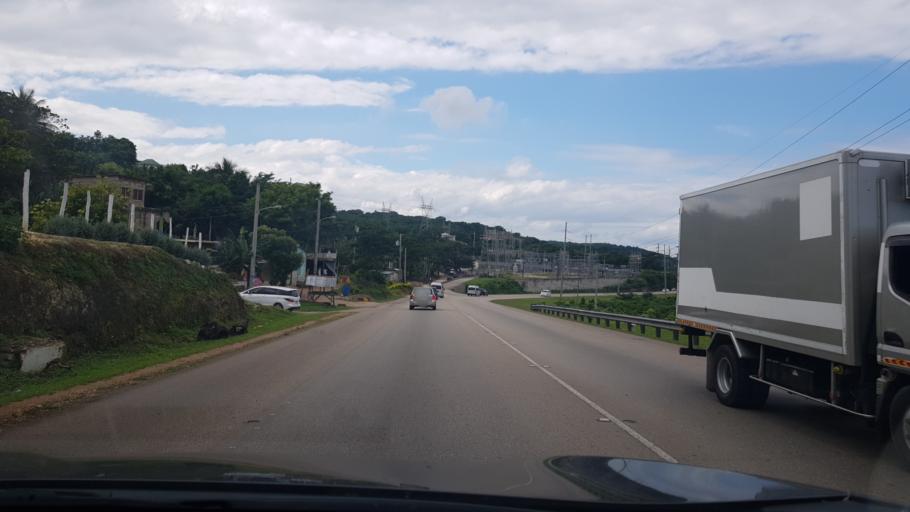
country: JM
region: Trelawny
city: Duncans
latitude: 18.4720
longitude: -77.5562
